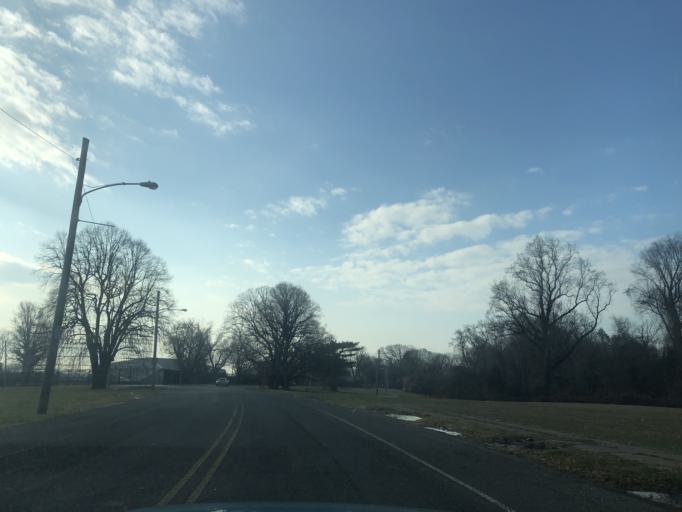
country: US
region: Pennsylvania
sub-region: Montgomery County
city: Bala-Cynwyd
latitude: 39.9867
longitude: -75.2226
